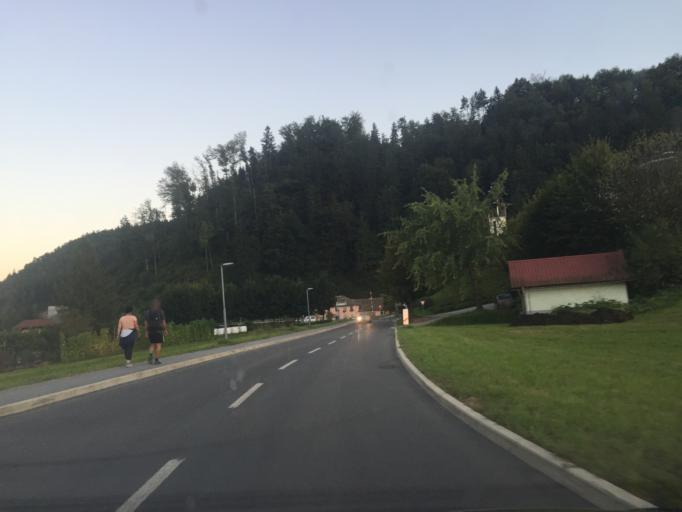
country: SI
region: Sostanj
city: Sostanj
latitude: 46.3824
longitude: 15.0294
